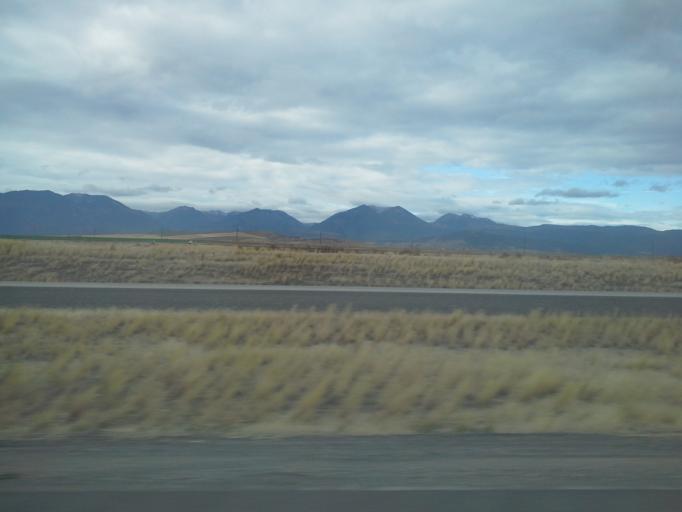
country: US
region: Oregon
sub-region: Union County
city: Union
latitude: 45.0002
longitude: -117.9050
